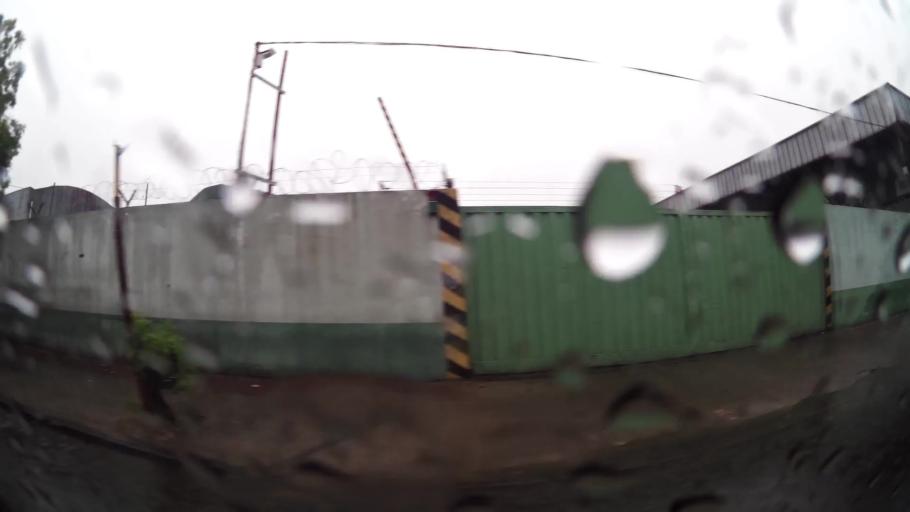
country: AR
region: Buenos Aires
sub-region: Partido de Avellaneda
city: Avellaneda
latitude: -34.6463
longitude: -58.4036
